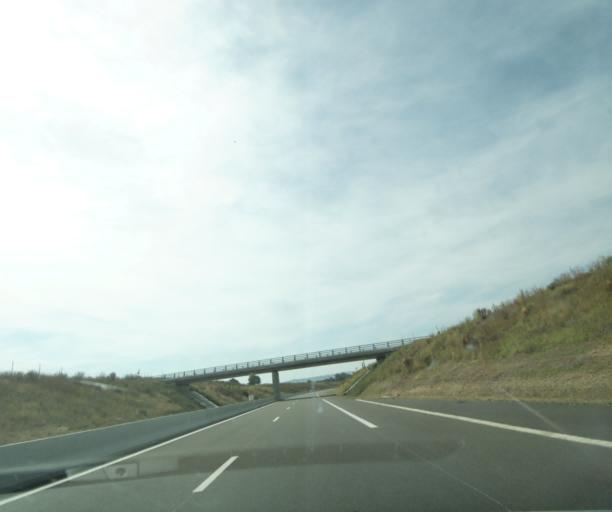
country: FR
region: Auvergne
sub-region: Departement de l'Allier
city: Gannat
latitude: 46.1069
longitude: 3.2609
